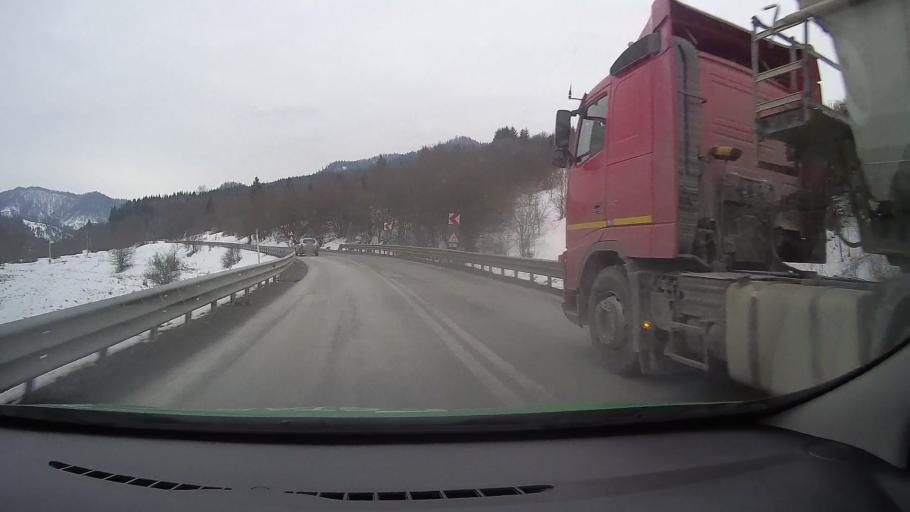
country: RO
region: Brasov
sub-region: Oras Predeal
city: Predeal
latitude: 45.5282
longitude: 25.4996
